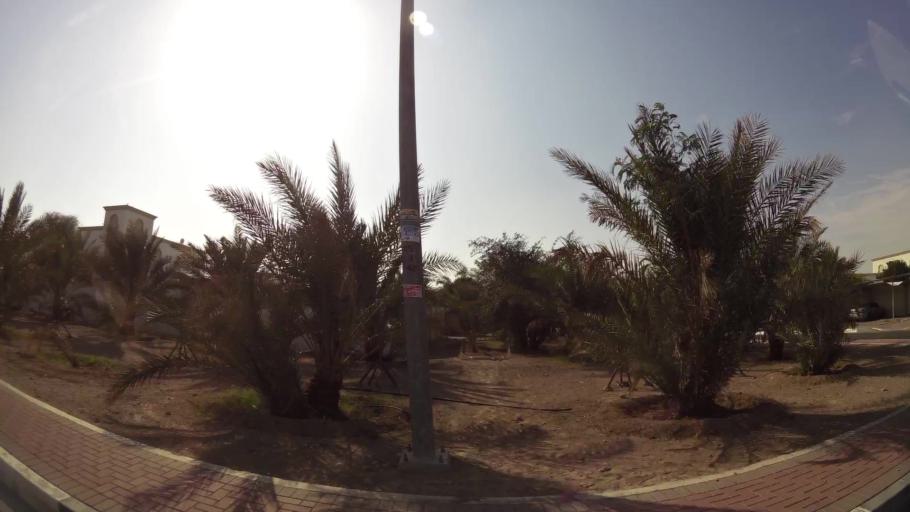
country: AE
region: Abu Dhabi
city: Al Ain
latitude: 24.0798
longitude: 55.8629
